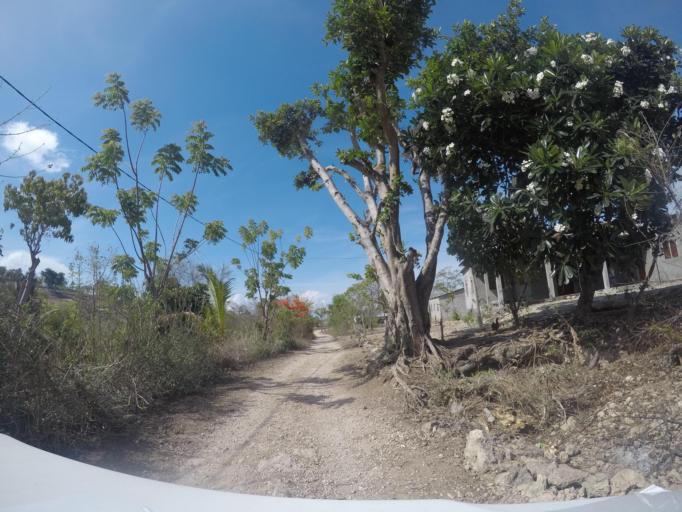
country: TL
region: Baucau
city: Baucau
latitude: -8.4628
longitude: 126.4697
